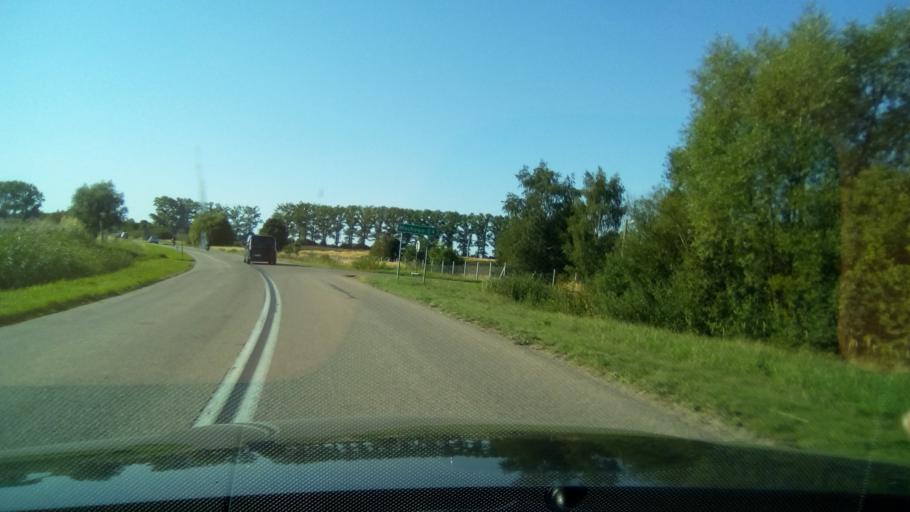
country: PL
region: West Pomeranian Voivodeship
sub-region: Powiat gryficki
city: Ploty
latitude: 53.8151
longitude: 15.1704
